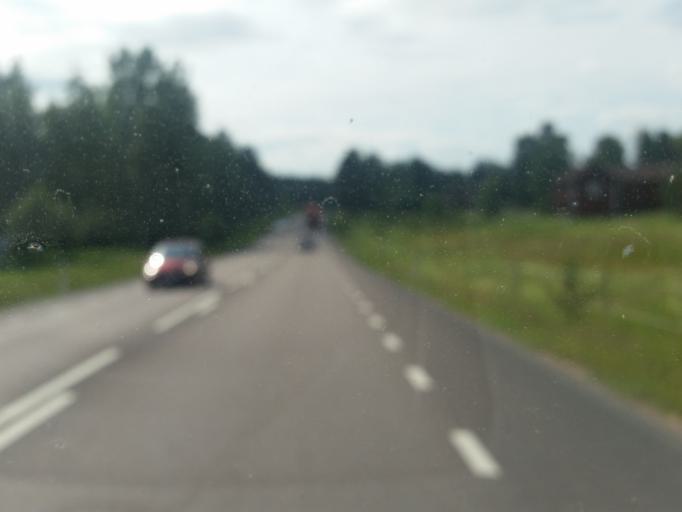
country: SE
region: Dalarna
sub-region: Gagnefs Kommun
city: Gagnef
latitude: 60.6358
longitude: 15.0576
